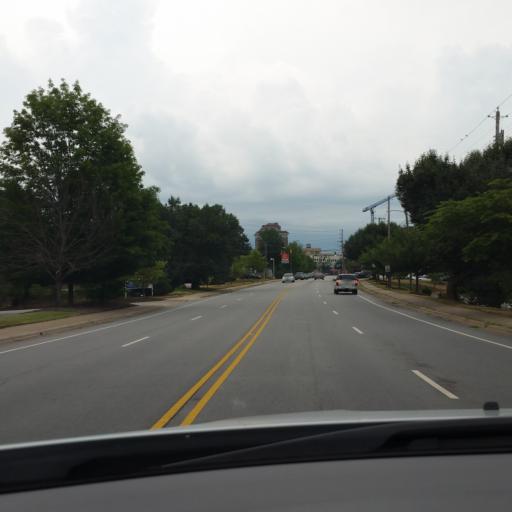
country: US
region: North Carolina
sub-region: Buncombe County
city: Asheville
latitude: 35.5896
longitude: -82.5564
